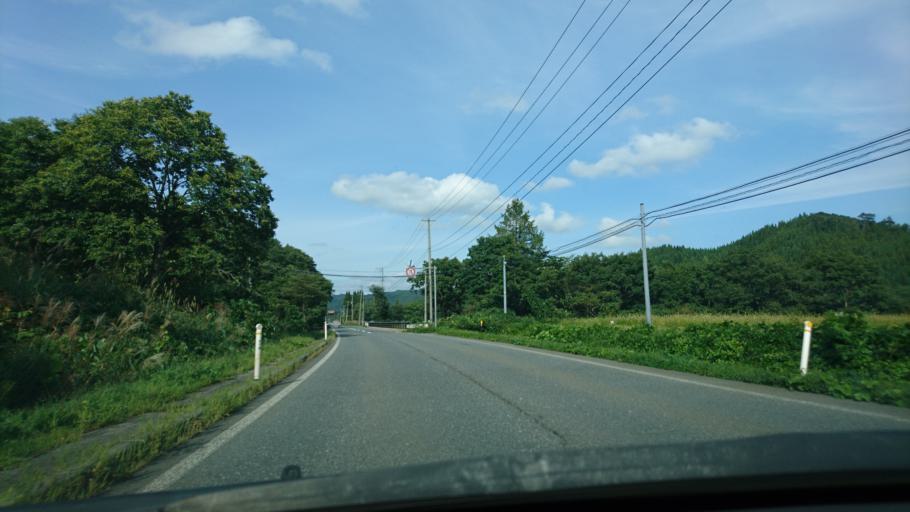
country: JP
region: Akita
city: Yokotemachi
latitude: 39.3044
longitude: 140.7425
